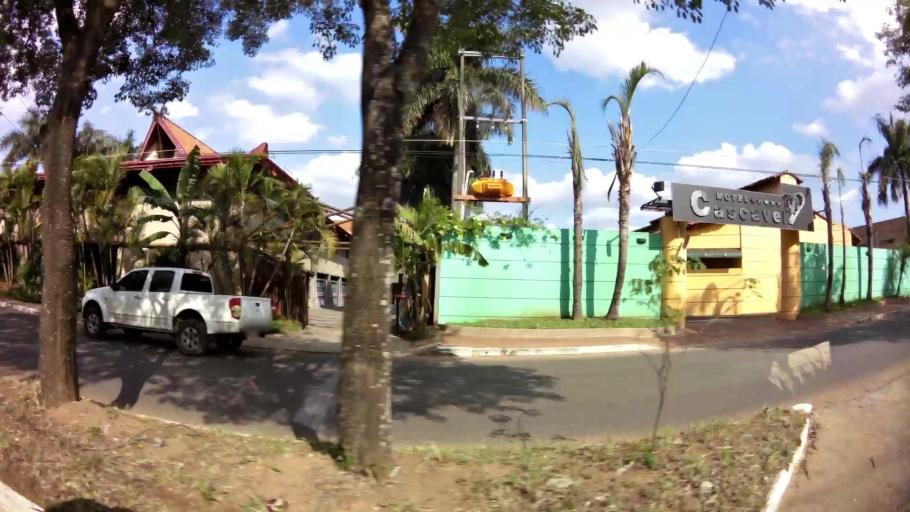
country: PY
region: Central
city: Fernando de la Mora
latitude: -25.3413
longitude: -57.5398
